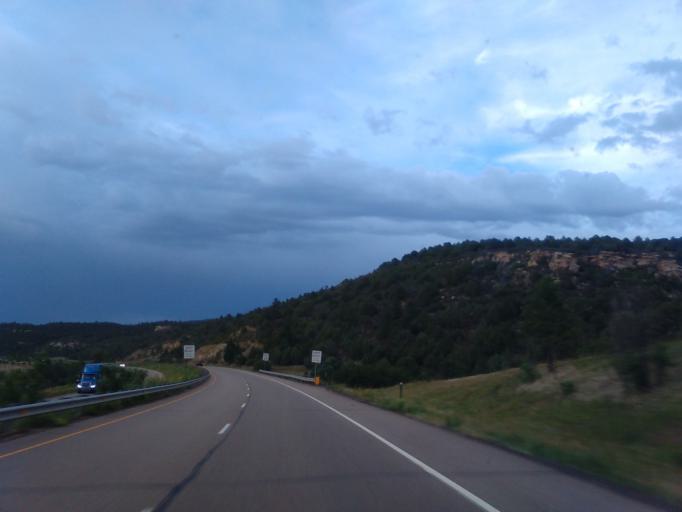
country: US
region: Colorado
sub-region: Las Animas County
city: Trinidad
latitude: 37.0646
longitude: -104.5197
